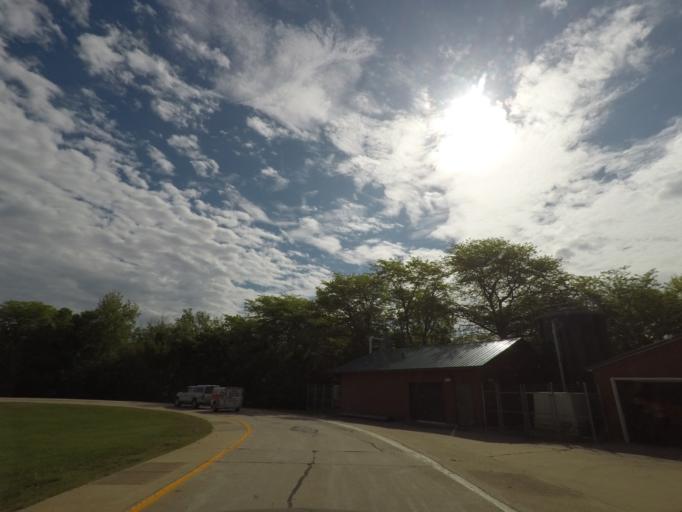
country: US
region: Illinois
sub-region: McLean County
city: Twin Grove
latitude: 40.3601
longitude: -89.1092
